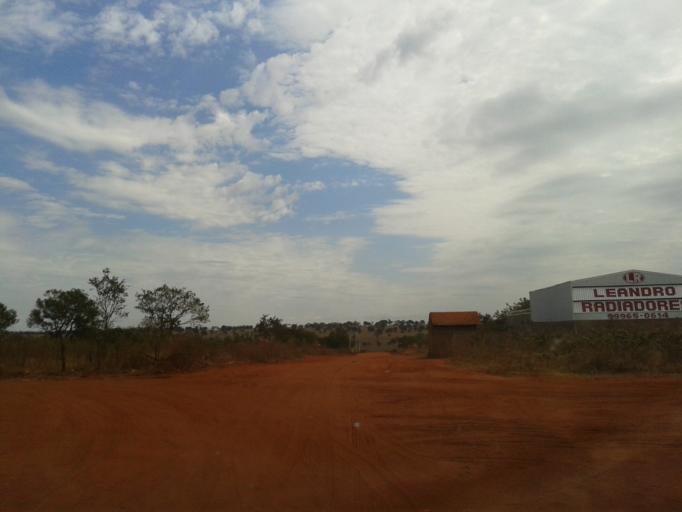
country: BR
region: Minas Gerais
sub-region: Santa Vitoria
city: Santa Vitoria
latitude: -18.8532
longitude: -50.1315
